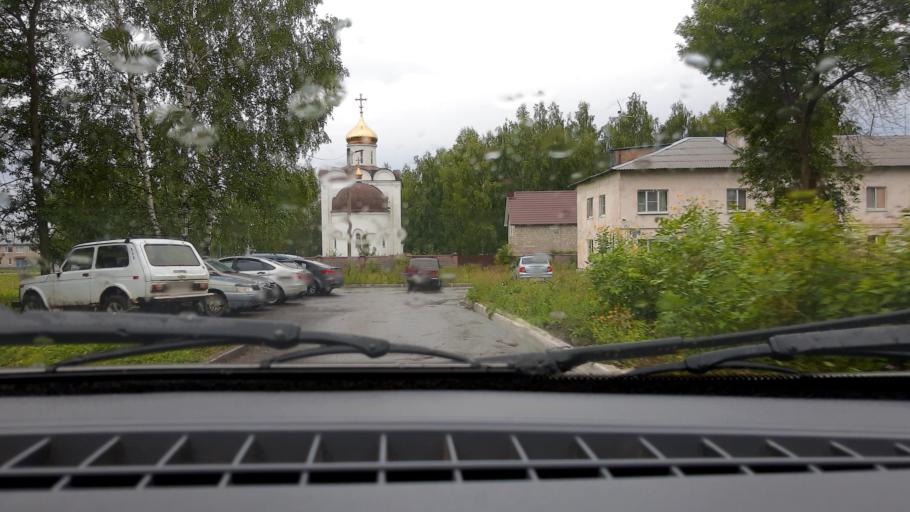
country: RU
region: Bashkortostan
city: Avdon
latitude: 54.8198
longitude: 55.6975
